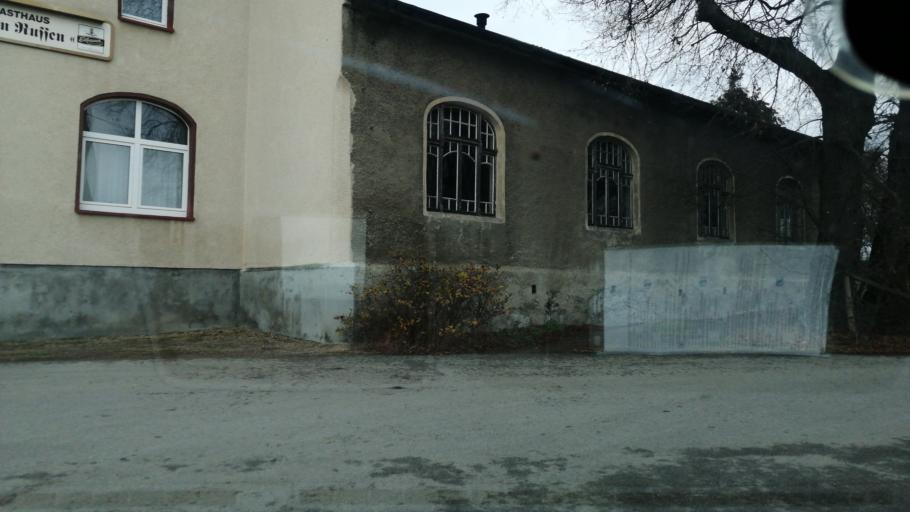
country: DE
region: Saxony
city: Bernstadt
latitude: 51.0540
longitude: 14.7960
